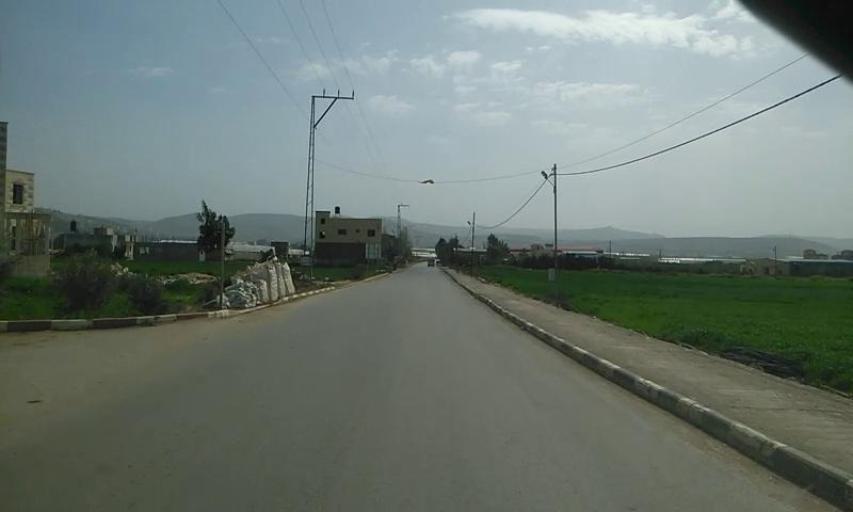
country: PS
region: West Bank
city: Birqin
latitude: 32.4461
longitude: 35.2619
